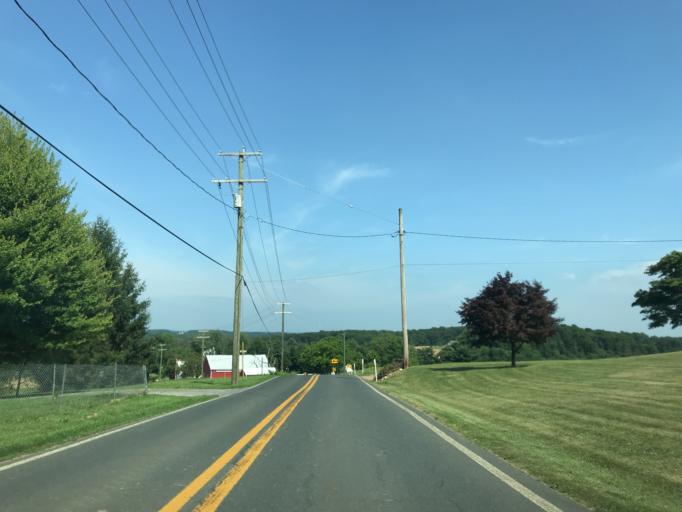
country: US
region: Maryland
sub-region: Carroll County
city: Manchester
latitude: 39.6697
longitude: -76.8710
